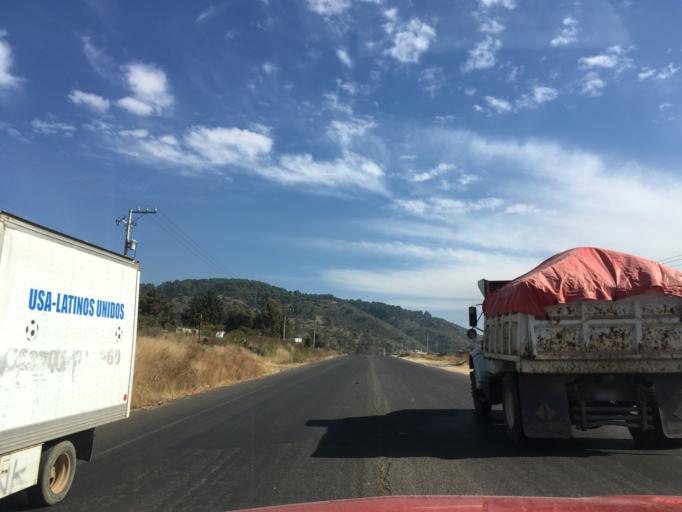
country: MX
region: Michoacan
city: Ciudad Hidalgo
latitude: 19.7033
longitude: -100.5721
